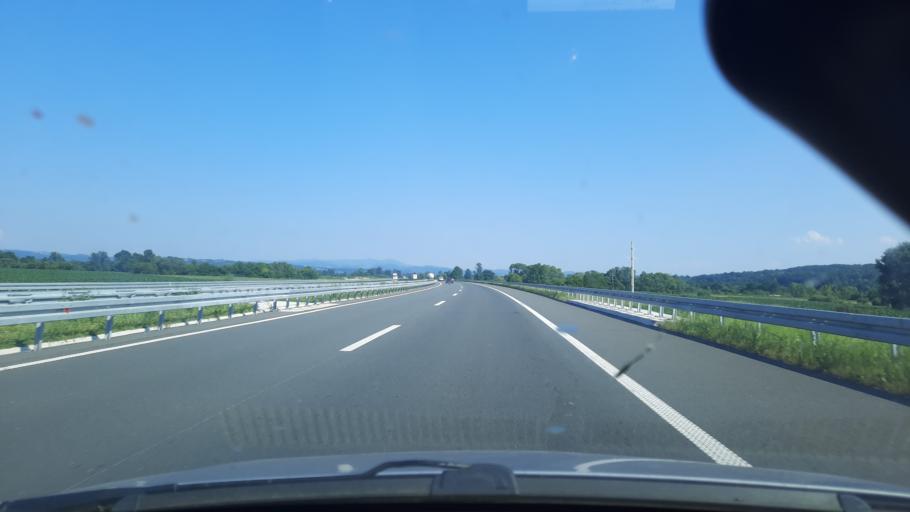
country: RS
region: Central Serbia
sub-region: Kolubarski Okrug
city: Lajkovac
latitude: 44.3123
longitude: 20.2183
